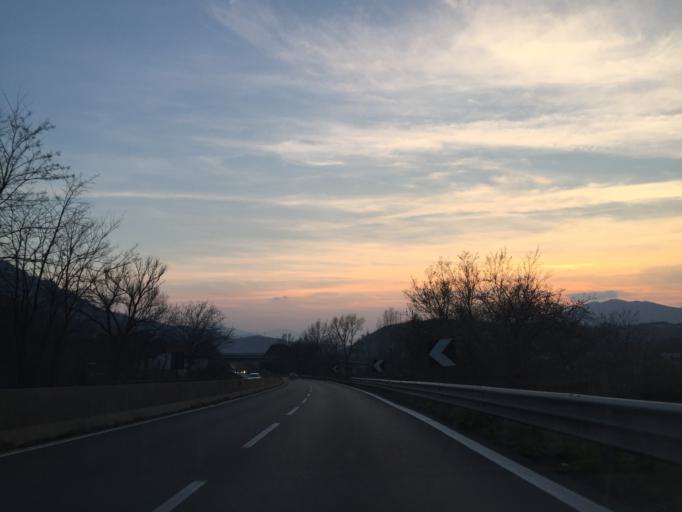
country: IT
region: Campania
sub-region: Provincia di Avellino
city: Solofra
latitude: 40.8328
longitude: 14.8217
